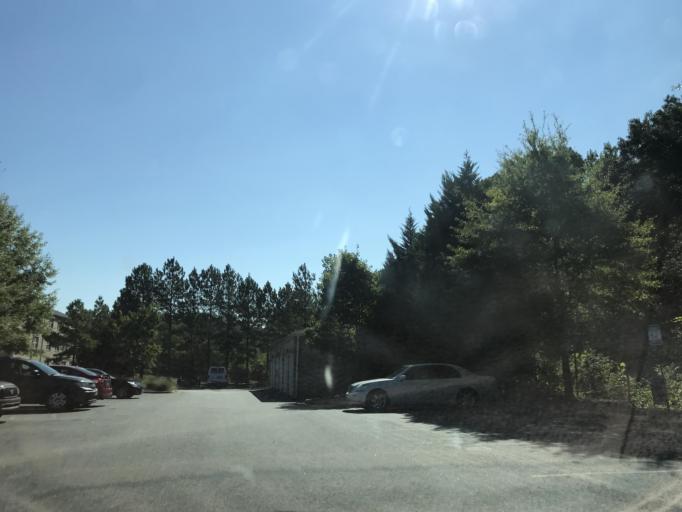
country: US
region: North Carolina
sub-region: Wake County
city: Raleigh
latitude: 35.7916
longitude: -78.5823
